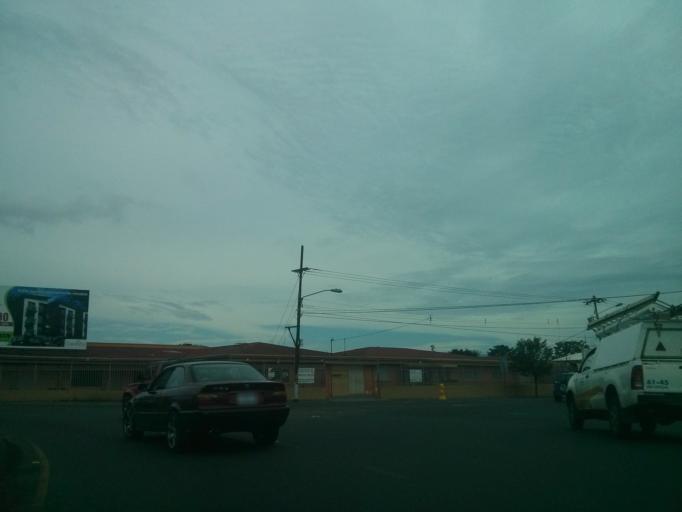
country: CR
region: San Jose
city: Alajuelita
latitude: 9.9106
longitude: -84.0852
